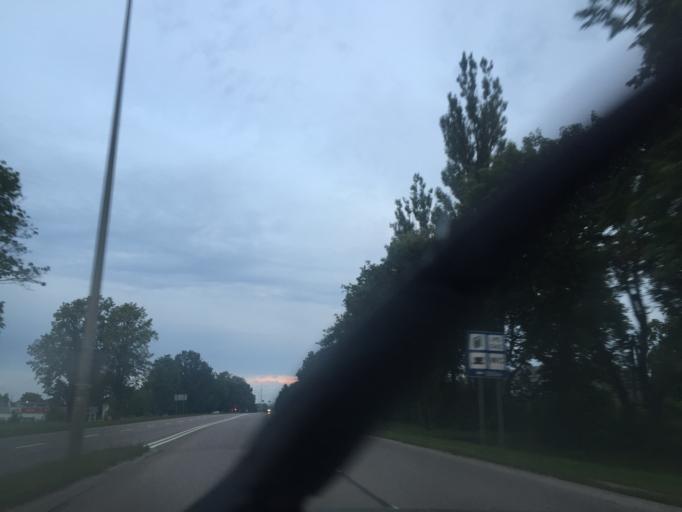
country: PL
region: Podlasie
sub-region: Bialystok
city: Bialystok
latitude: 53.1450
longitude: 23.0790
